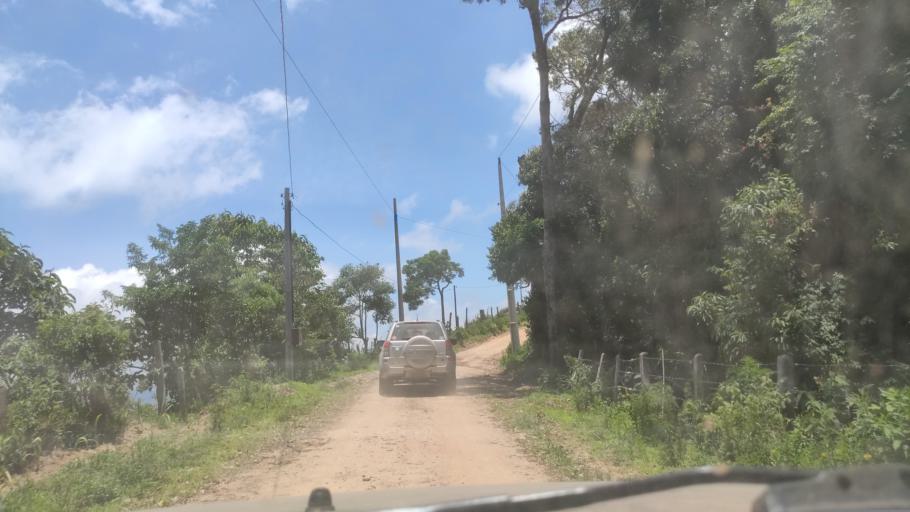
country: BR
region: Minas Gerais
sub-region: Cambui
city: Cambui
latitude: -22.6818
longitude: -45.9646
